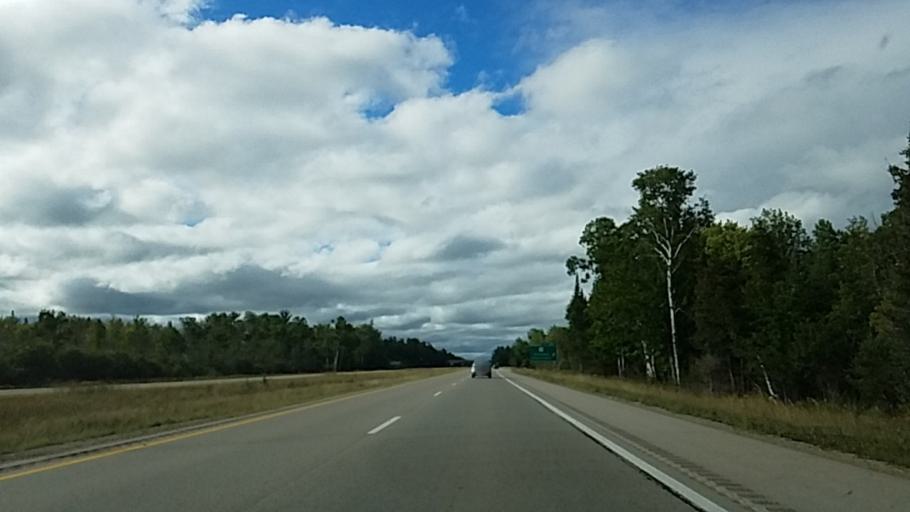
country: US
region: Michigan
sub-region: Mackinac County
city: Saint Ignace
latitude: 45.7403
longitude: -84.7289
